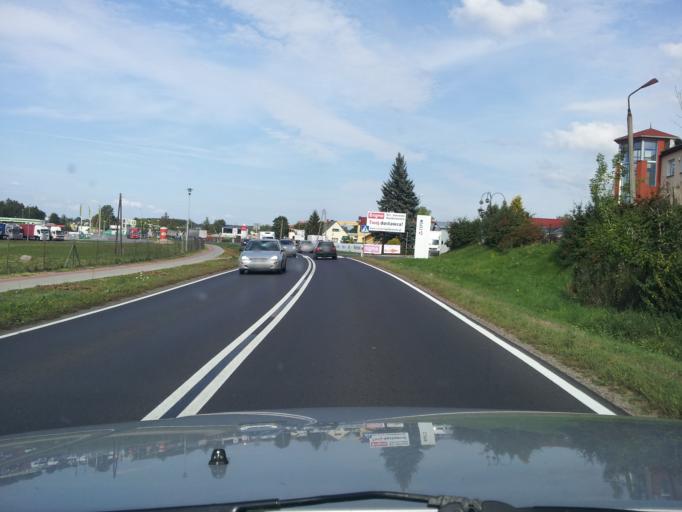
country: PL
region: Warmian-Masurian Voivodeship
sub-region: Powiat nowomiejski
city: Kurzetnik
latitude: 53.4056
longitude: 19.5923
